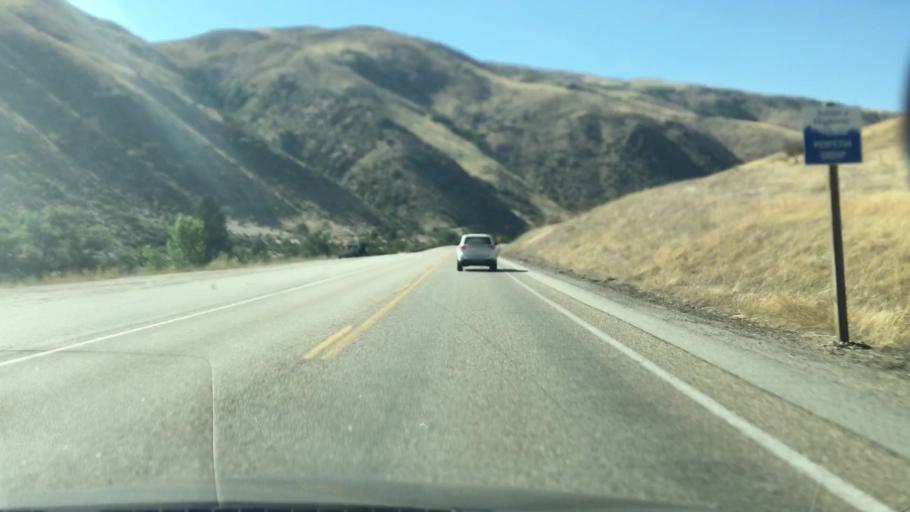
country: US
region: Idaho
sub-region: Ada County
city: Eagle
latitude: 43.9371
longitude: -116.1912
